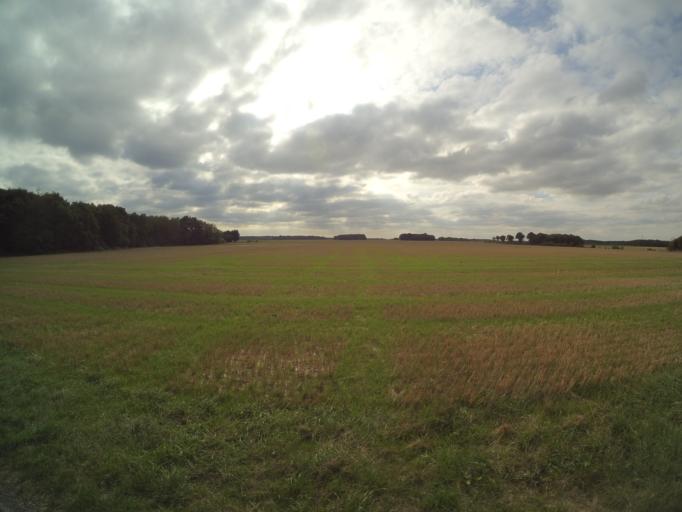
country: FR
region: Centre
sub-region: Departement d'Indre-et-Loire
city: Nazelles-Negron
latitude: 47.4812
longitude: 0.9406
